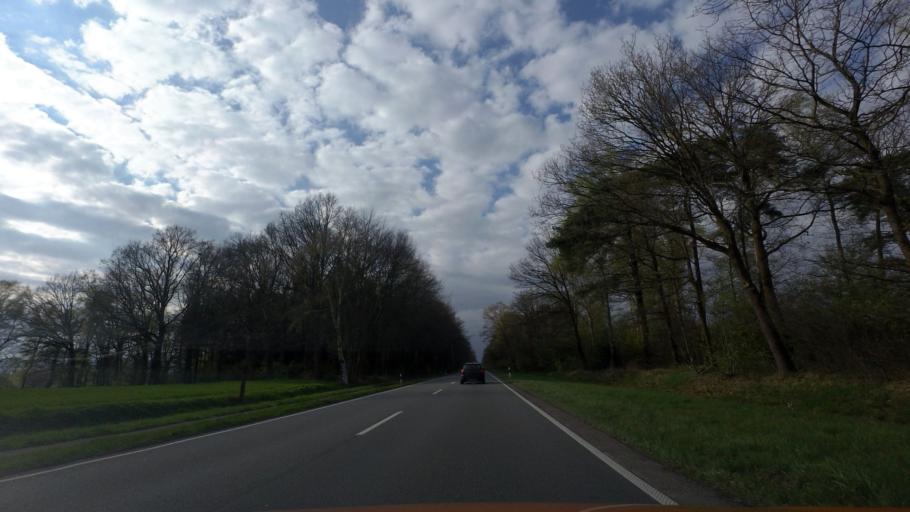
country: DE
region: Lower Saxony
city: Friesoythe
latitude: 52.9892
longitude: 7.8877
